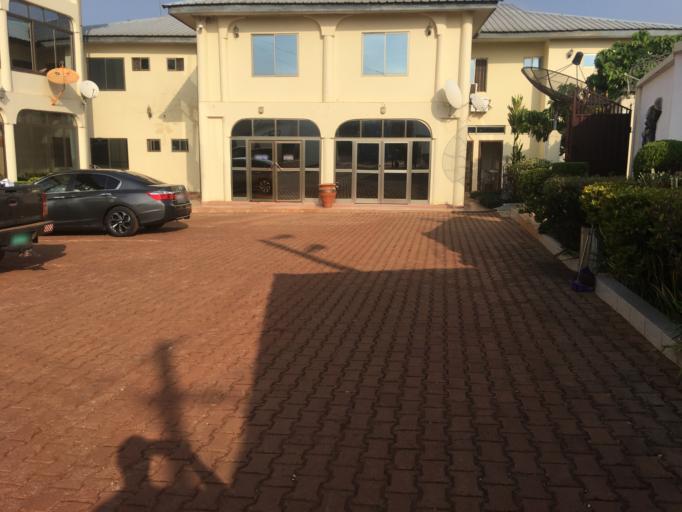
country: GH
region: Brong-Ahafo
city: Techiman
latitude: 7.5917
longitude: -1.9419
